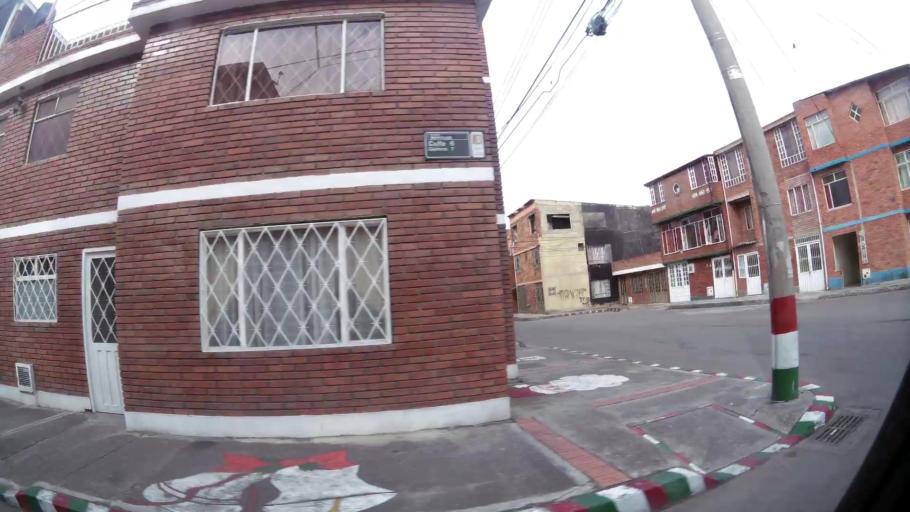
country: CO
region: Cundinamarca
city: Funza
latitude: 4.7069
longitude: -74.2145
